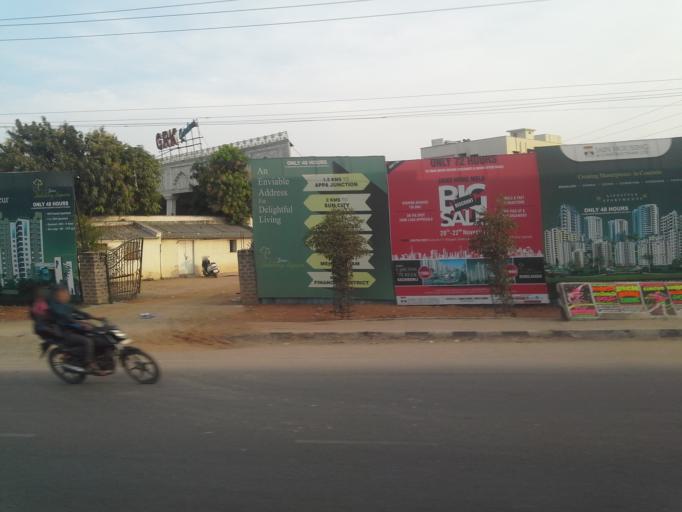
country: IN
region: Telangana
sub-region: Hyderabad
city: Hyderabad
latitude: 17.3574
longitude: 78.3842
